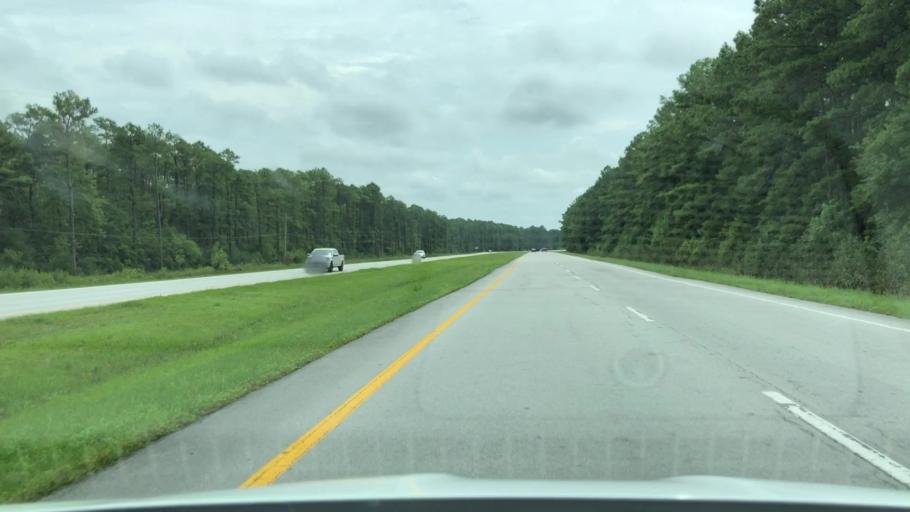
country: US
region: North Carolina
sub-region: Craven County
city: Havelock
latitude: 34.8500
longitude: -76.8876
